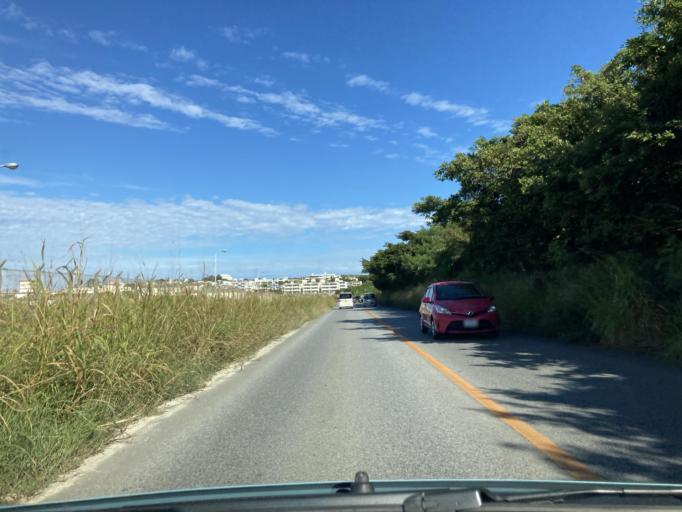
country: JP
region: Okinawa
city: Okinawa
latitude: 26.3748
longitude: 127.7459
